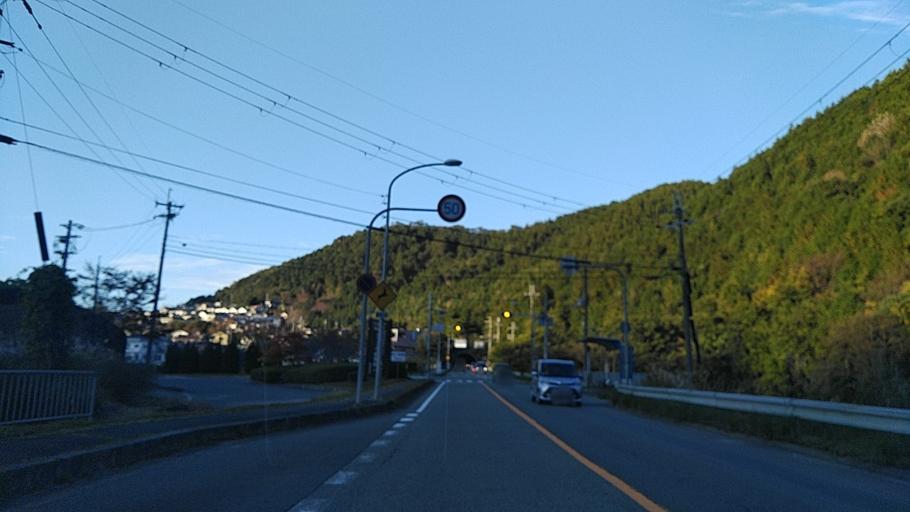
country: JP
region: Osaka
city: Ikeda
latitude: 34.9432
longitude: 135.4111
